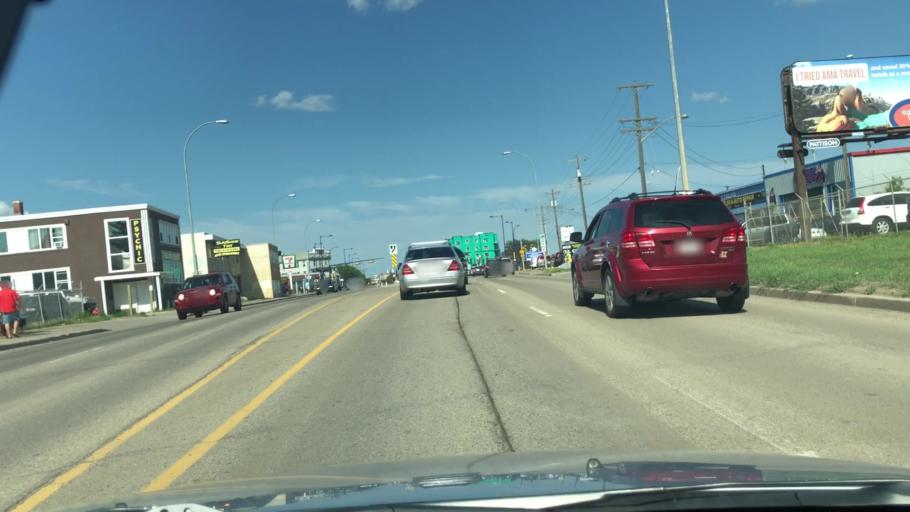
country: CA
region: Alberta
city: Edmonton
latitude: 53.5838
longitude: -113.4457
